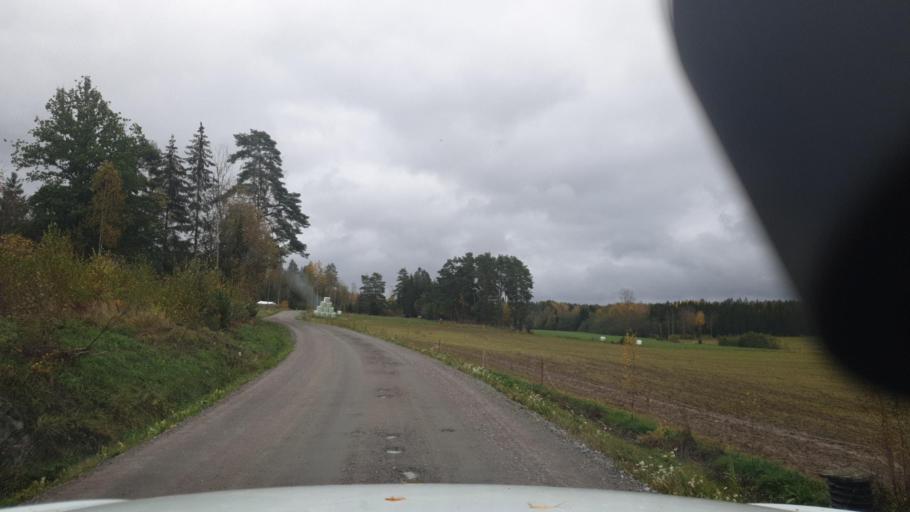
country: SE
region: Vaermland
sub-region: Karlstads Kommun
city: Edsvalla
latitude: 59.4979
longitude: 13.1847
